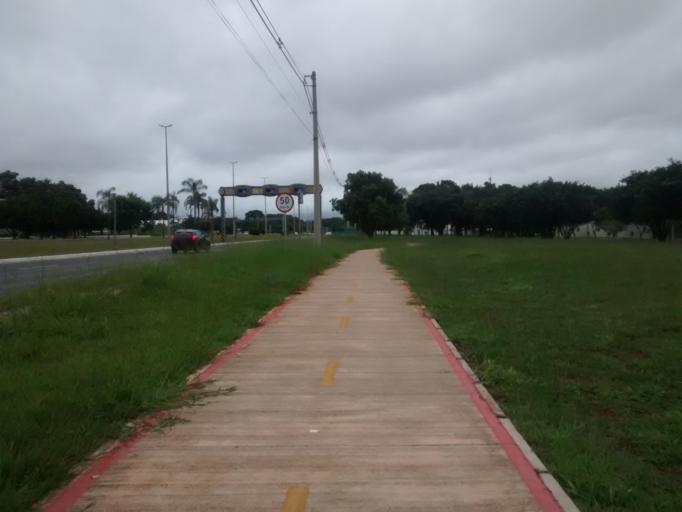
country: BR
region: Federal District
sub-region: Brasilia
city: Brasilia
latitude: -15.7697
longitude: -47.8723
